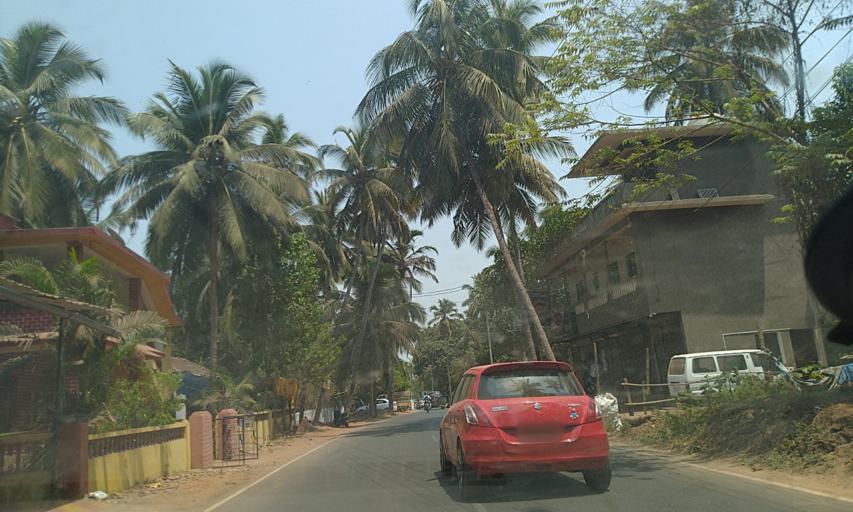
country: IN
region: Goa
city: Calangute
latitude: 15.5477
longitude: 73.7675
